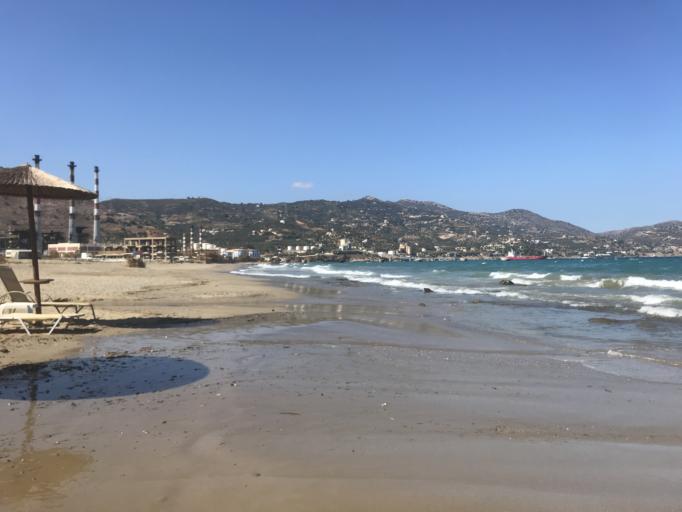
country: GR
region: Crete
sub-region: Nomos Irakleiou
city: Gazi
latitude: 35.3407
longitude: 25.0575
